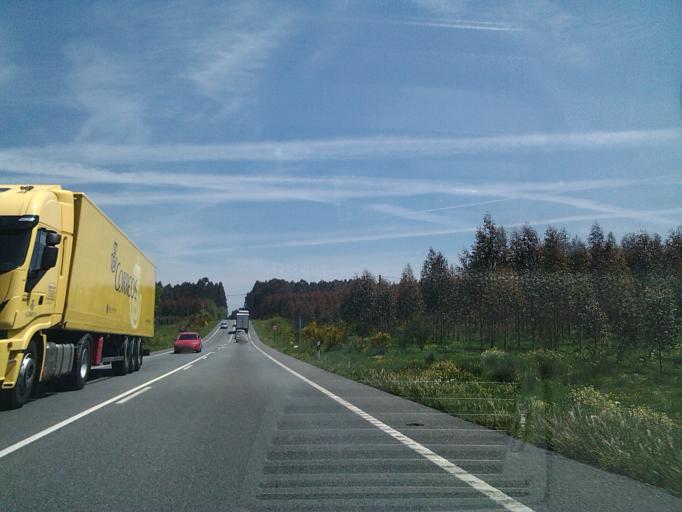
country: ES
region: Galicia
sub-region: Provincia da Coruna
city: Curtis
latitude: 43.1204
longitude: -8.0802
